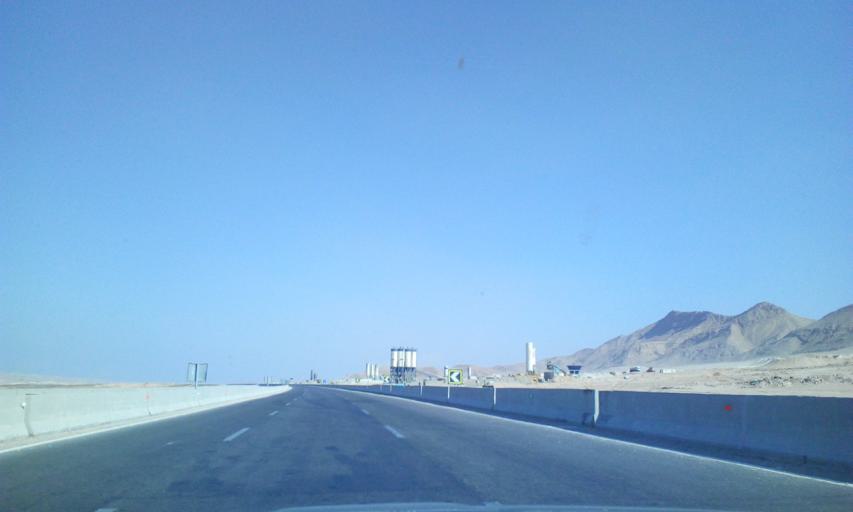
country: EG
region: As Suways
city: Ain Sukhna
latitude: 29.4482
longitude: 32.3446
